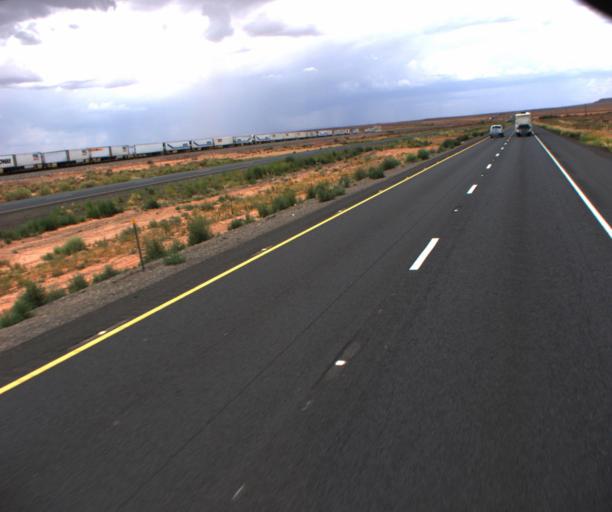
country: US
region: Arizona
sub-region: Coconino County
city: LeChee
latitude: 35.0462
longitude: -110.7621
